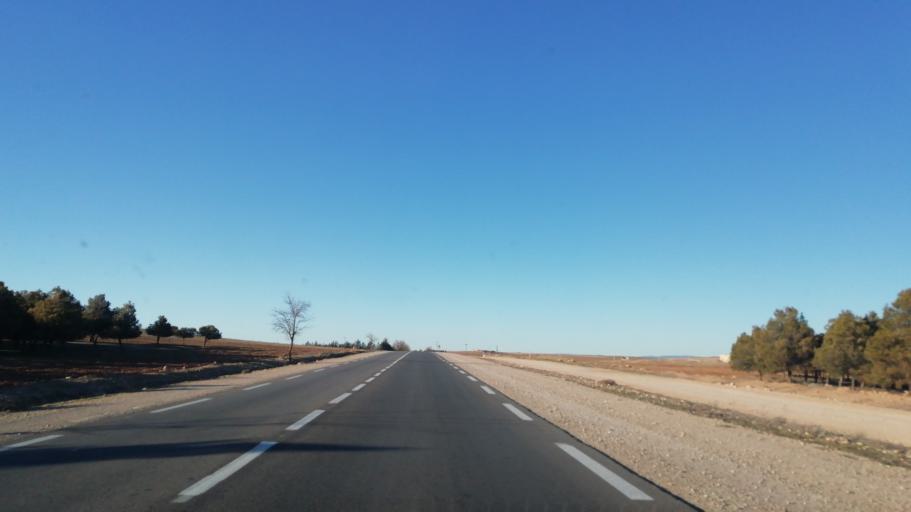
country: DZ
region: Tlemcen
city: Sebdou
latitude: 34.5154
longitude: -1.2858
